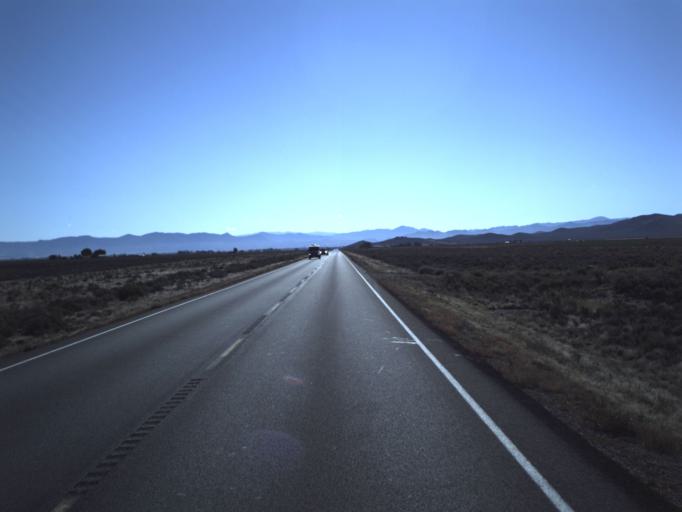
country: US
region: Utah
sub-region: Washington County
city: Enterprise
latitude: 37.7617
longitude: -113.8037
